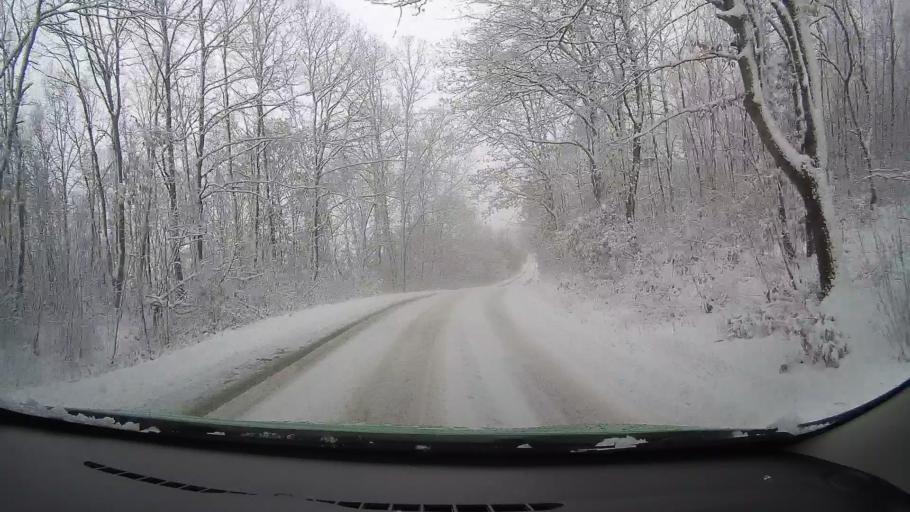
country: RO
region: Hunedoara
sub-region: Municipiul Deva
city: Deva
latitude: 45.8497
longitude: 22.8764
